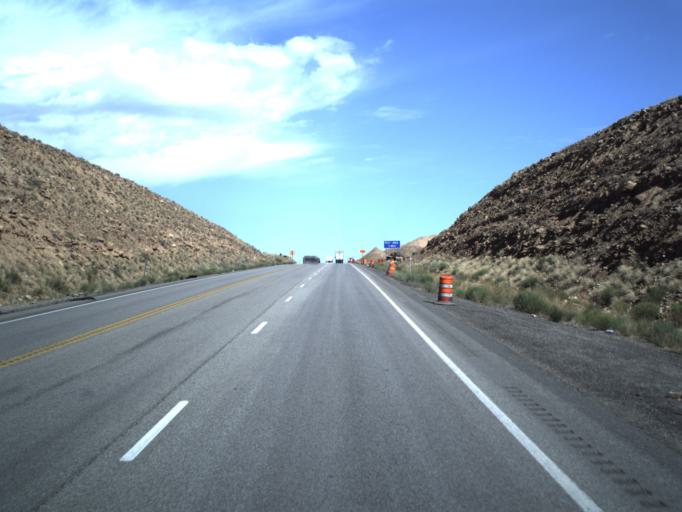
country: US
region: Utah
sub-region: Carbon County
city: East Carbon City
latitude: 39.3960
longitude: -110.4192
